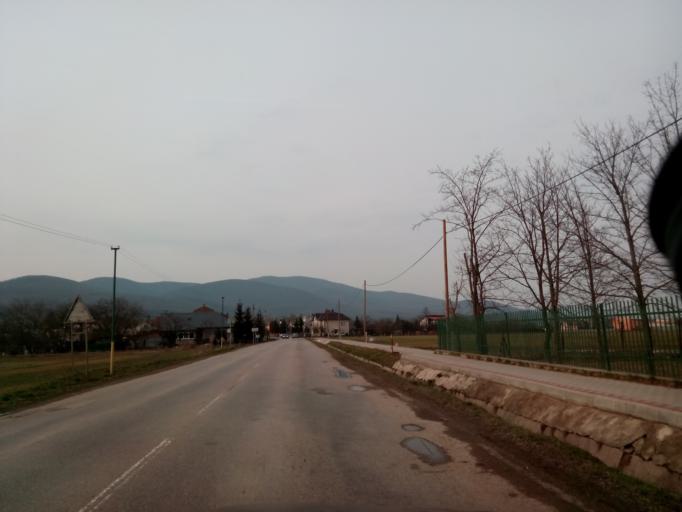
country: SK
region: Kosicky
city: Secovce
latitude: 48.6434
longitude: 21.5781
